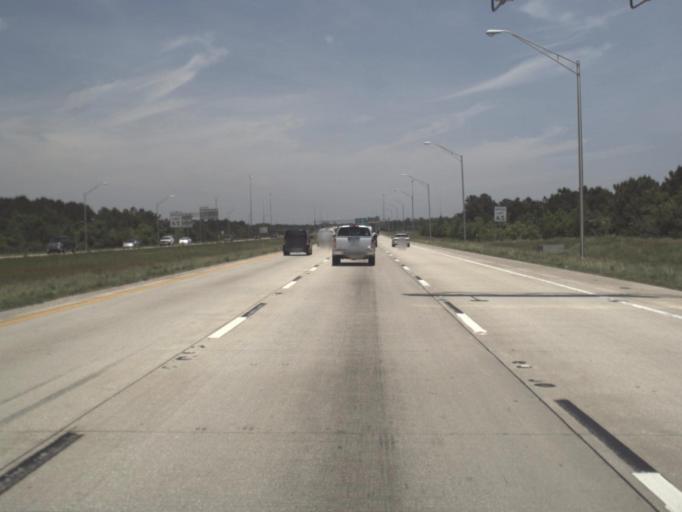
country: US
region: Florida
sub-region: Saint Johns County
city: Ponte Vedra Beach
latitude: 30.2248
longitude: -81.5139
